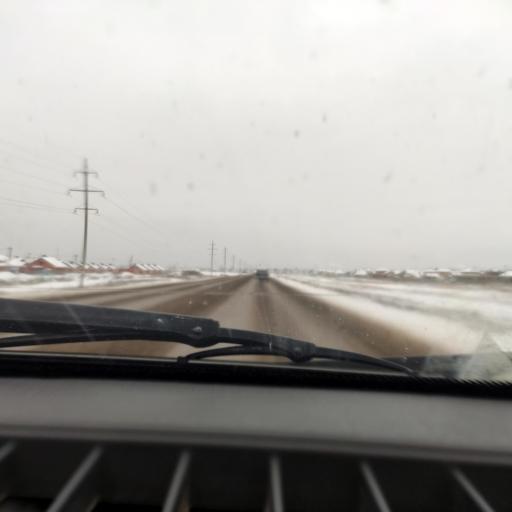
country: RU
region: Bashkortostan
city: Ufa
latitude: 54.6293
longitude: 55.8992
